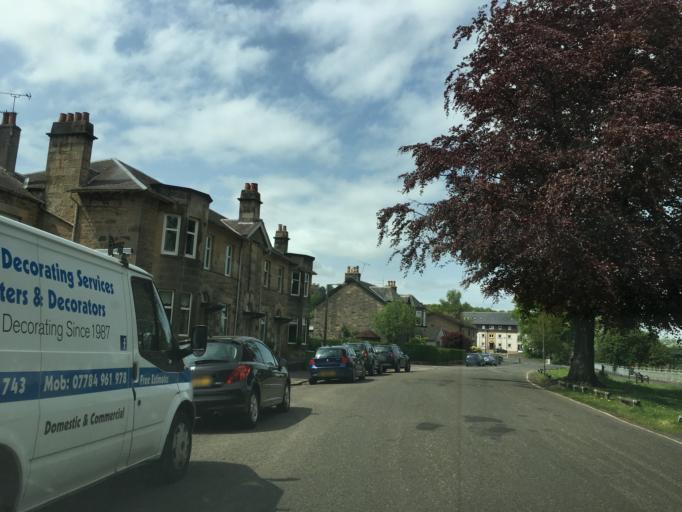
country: GB
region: Scotland
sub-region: Stirling
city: Stirling
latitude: 56.1261
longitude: -3.9314
